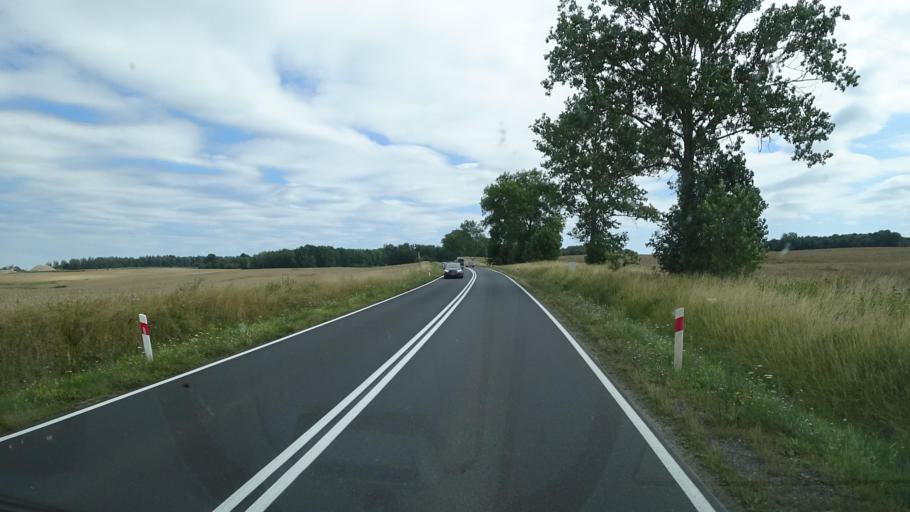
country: PL
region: Warmian-Masurian Voivodeship
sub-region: Powiat elcki
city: Stare Juchy
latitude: 53.7928
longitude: 22.2104
